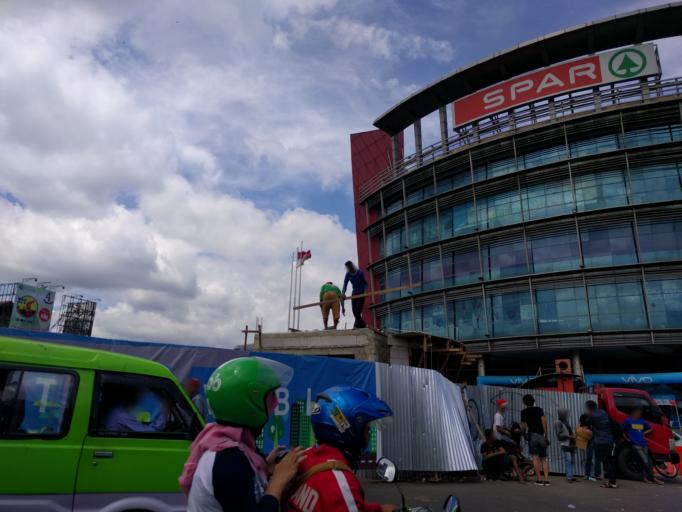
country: ID
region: West Java
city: Bogor
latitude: -6.6042
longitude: 106.7966
